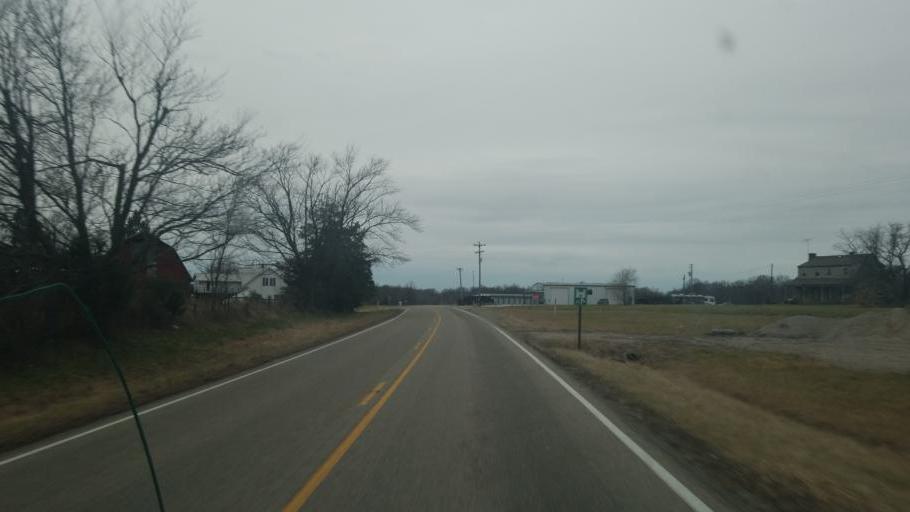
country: US
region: Indiana
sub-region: Clay County
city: Middlebury
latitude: 39.3708
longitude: -86.9782
